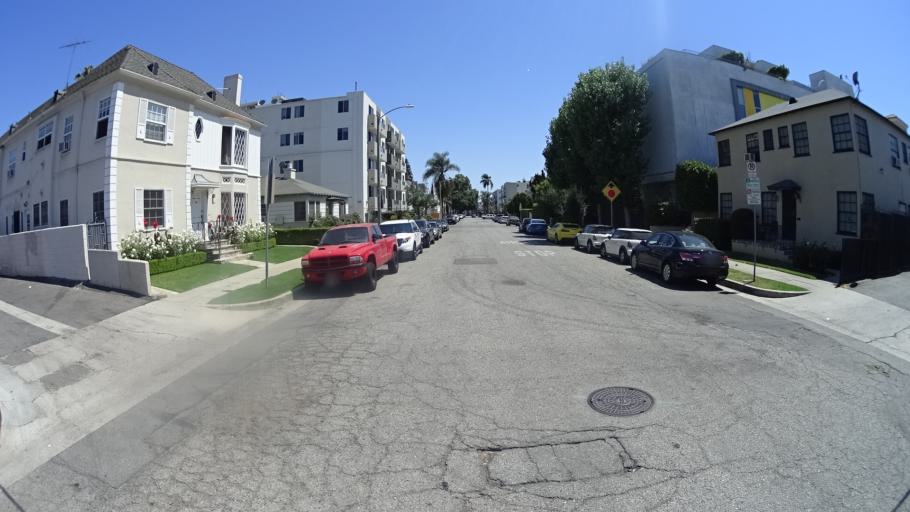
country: US
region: California
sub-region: Los Angeles County
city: West Hollywood
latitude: 34.0756
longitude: -118.3721
